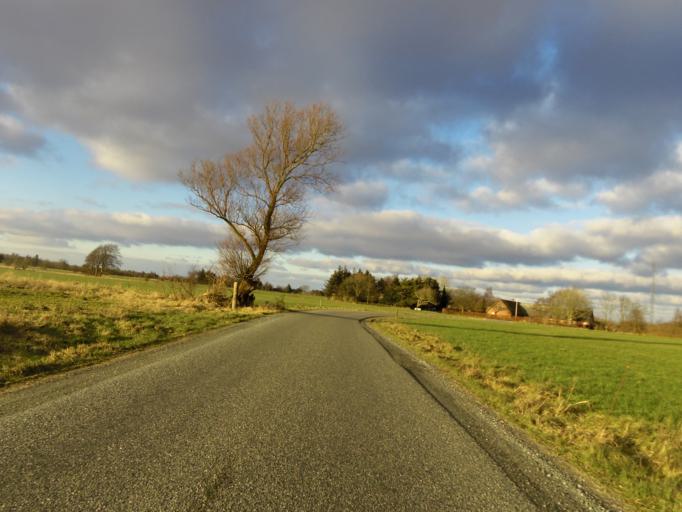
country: DK
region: South Denmark
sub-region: Esbjerg Kommune
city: Ribe
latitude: 55.2892
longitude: 8.8470
